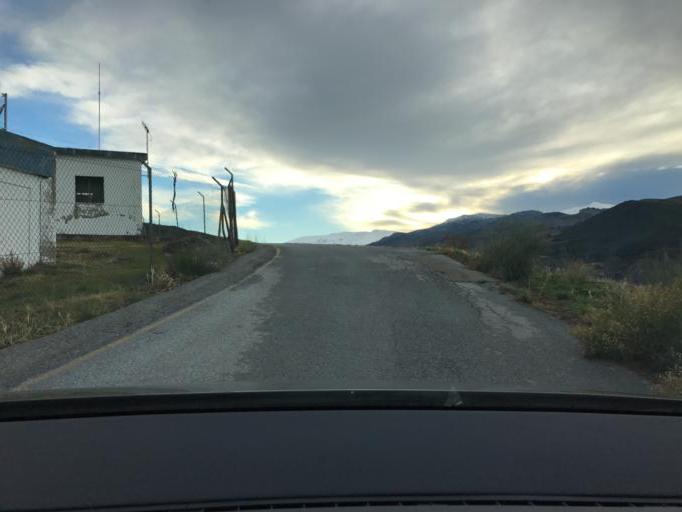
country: ES
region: Andalusia
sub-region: Provincia de Granada
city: Cenes de la Vega
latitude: 37.1667
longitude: -3.5377
